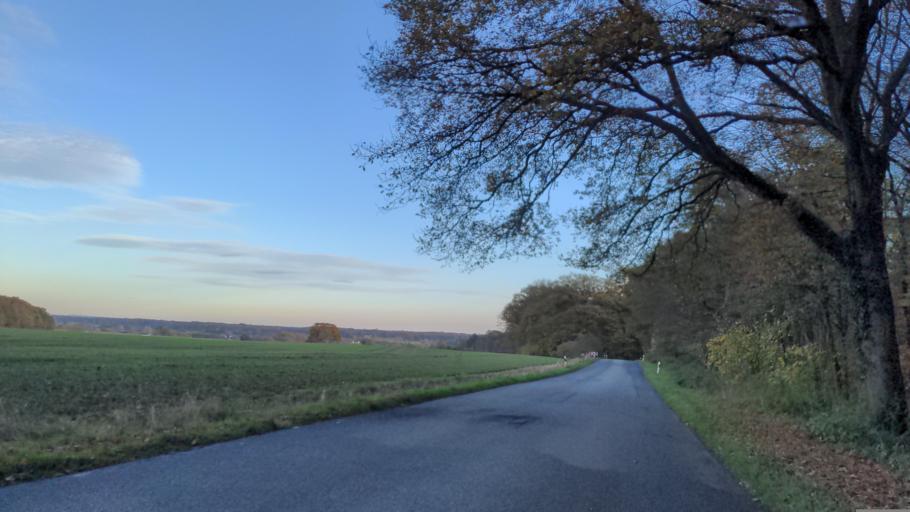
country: DE
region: Schleswig-Holstein
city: Heidekamp
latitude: 53.8543
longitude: 10.4721
